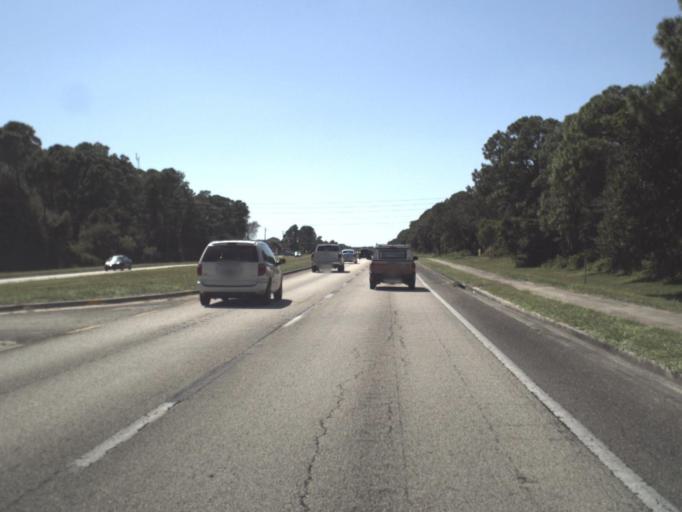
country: US
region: Florida
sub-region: Sarasota County
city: North Port
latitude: 27.0032
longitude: -82.1748
